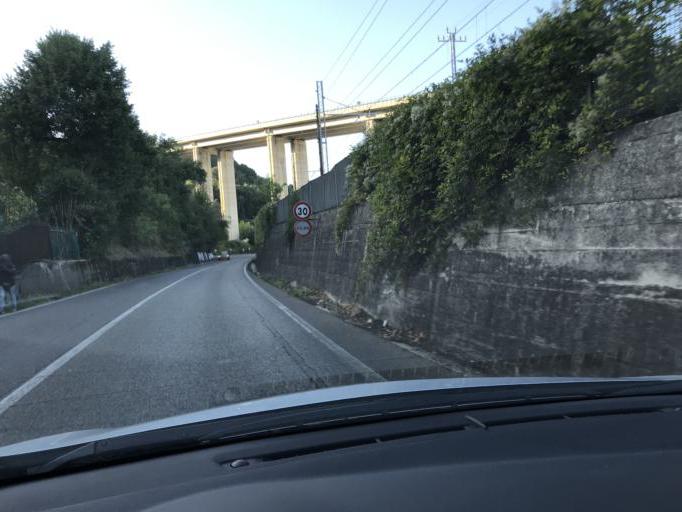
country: IT
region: Latium
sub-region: Provincia di Viterbo
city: Orte
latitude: 42.4499
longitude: 12.3894
